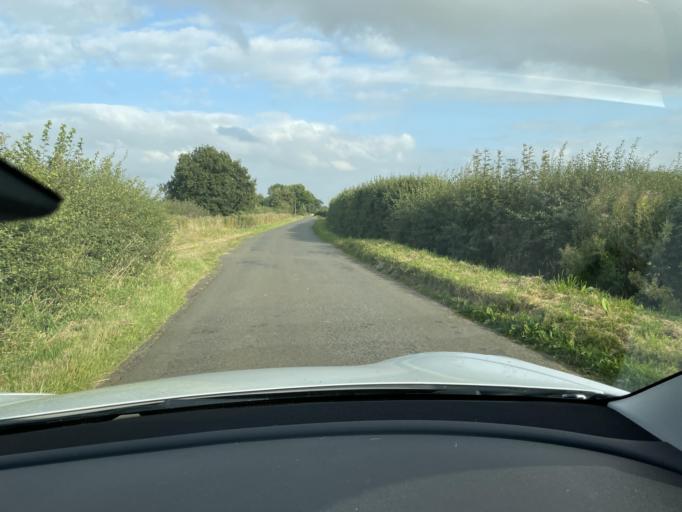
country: GB
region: England
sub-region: Northamptonshire
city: Long Buckby
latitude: 52.4187
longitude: -1.0354
